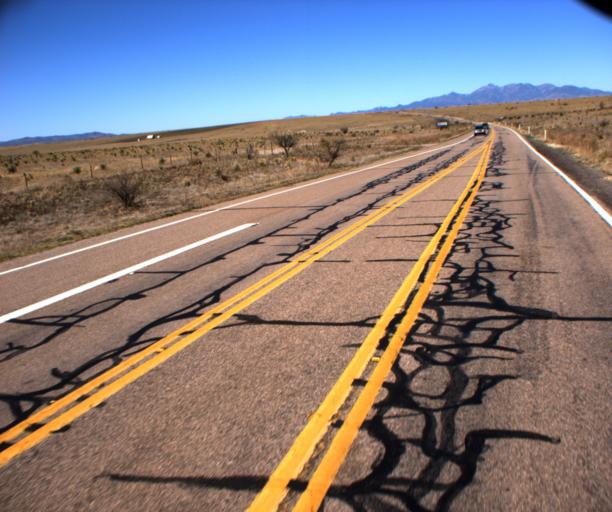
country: US
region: Arizona
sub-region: Cochise County
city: Huachuca City
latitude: 31.7240
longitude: -110.5249
